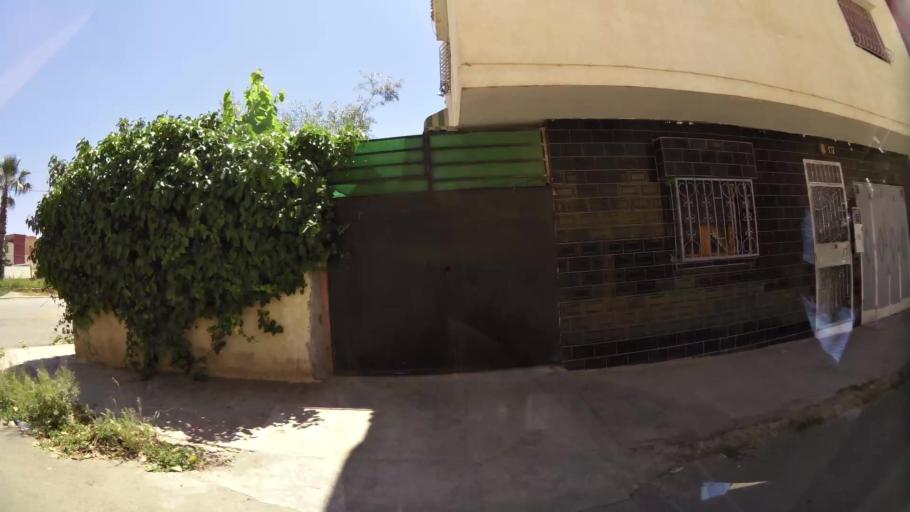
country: MA
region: Oriental
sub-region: Oujda-Angad
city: Oujda
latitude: 34.6581
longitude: -1.9287
